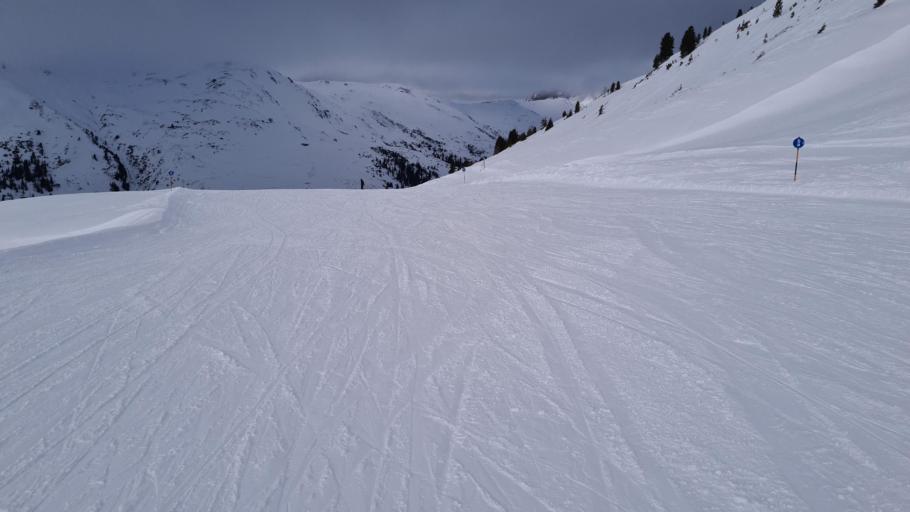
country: AT
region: Salzburg
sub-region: Politischer Bezirk Zell am See
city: Neukirchen am Grossvenediger
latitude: 47.2919
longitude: 12.2934
